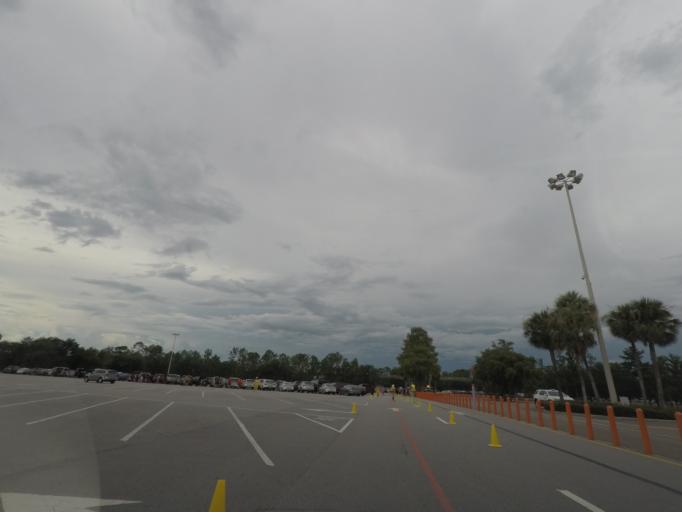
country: US
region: Florida
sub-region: Osceola County
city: Celebration
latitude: 28.4004
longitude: -81.5767
